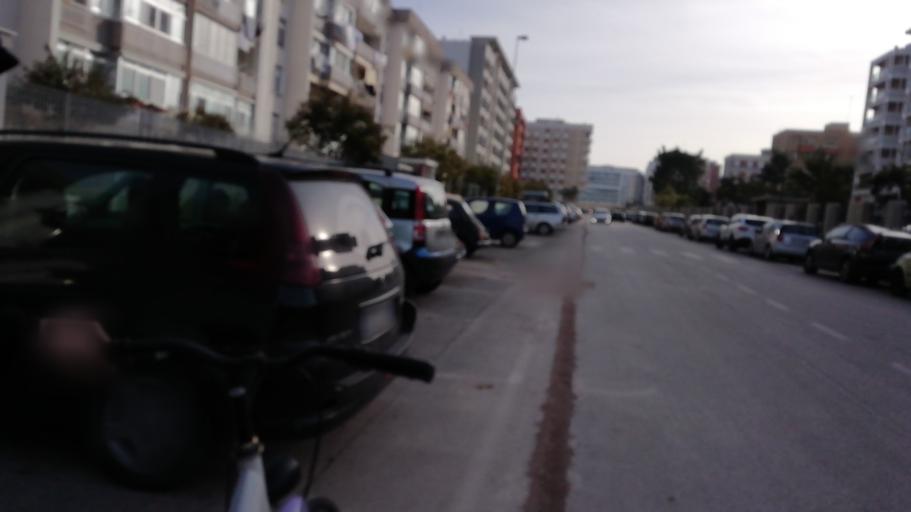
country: IT
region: Apulia
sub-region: Provincia di Bari
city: Triggiano
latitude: 41.1058
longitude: 16.9153
